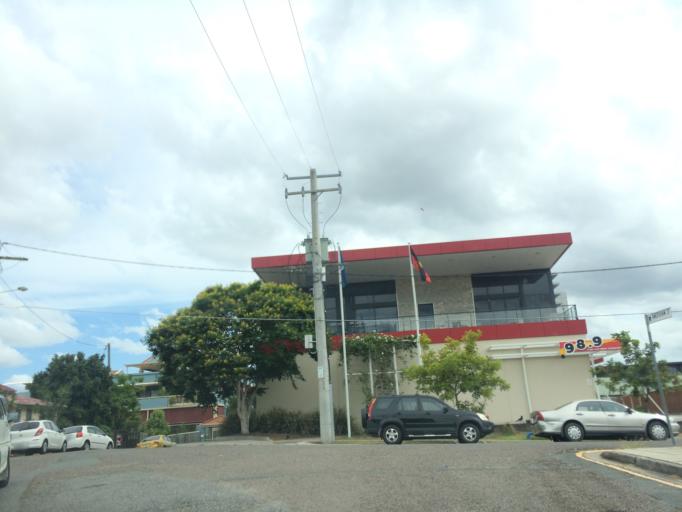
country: AU
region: Queensland
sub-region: Brisbane
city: South Brisbane
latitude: -27.4794
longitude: 153.0108
